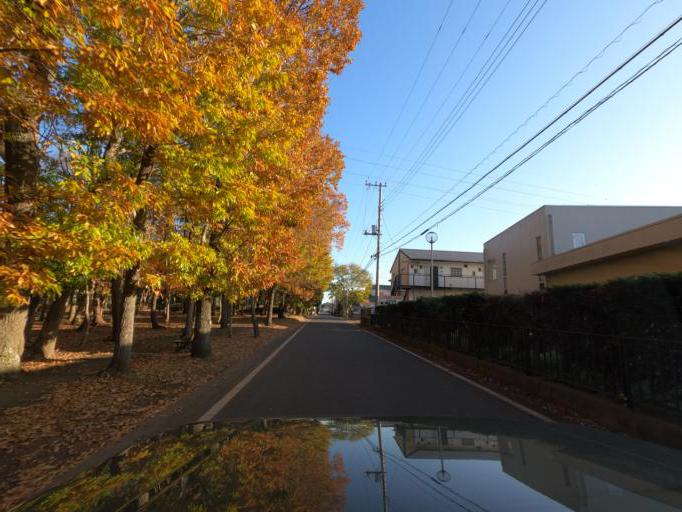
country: JP
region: Ibaraki
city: Naka
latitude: 36.0510
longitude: 140.1297
